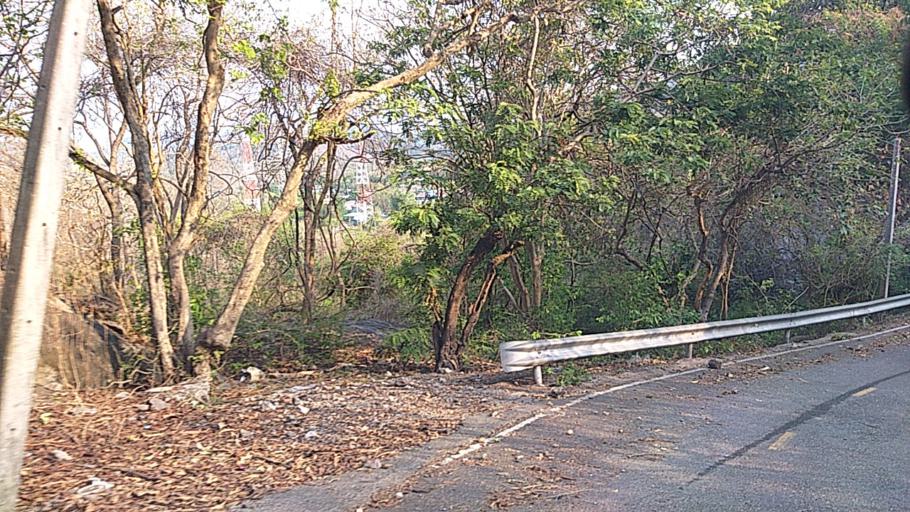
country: TH
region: Sara Buri
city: Saraburi
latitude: 14.4609
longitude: 100.9507
